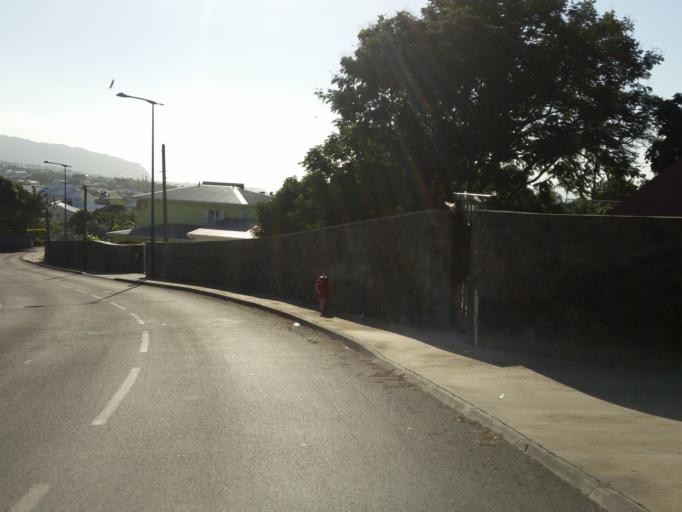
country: RE
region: Reunion
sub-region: Reunion
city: Sainte-Marie
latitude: -20.9231
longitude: 55.5178
